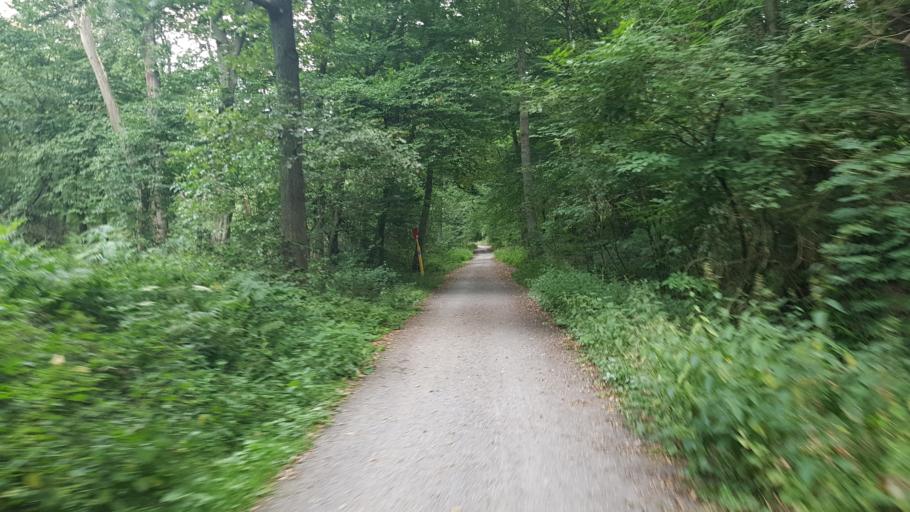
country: DE
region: North Rhine-Westphalia
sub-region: Regierungsbezirk Dusseldorf
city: Duisburg
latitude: 51.4167
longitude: 6.8043
